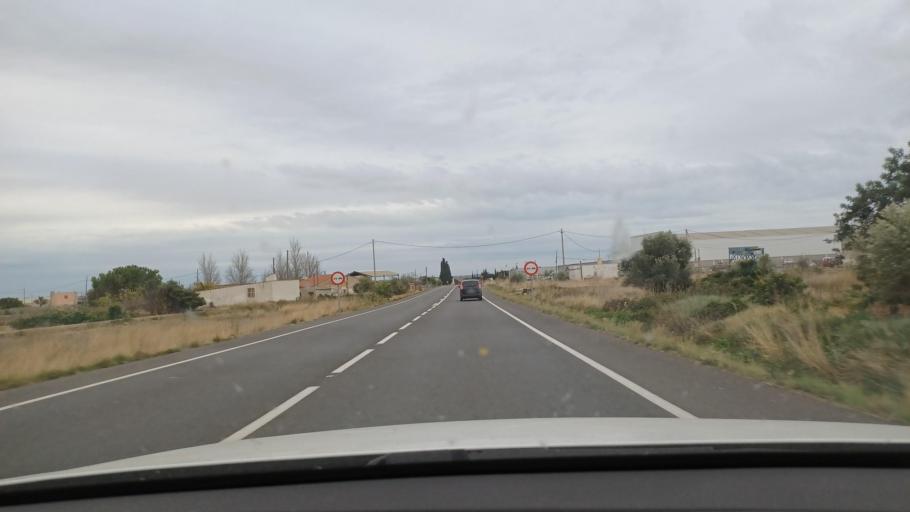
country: ES
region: Catalonia
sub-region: Provincia de Tarragona
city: Amposta
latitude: 40.6989
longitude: 0.5694
